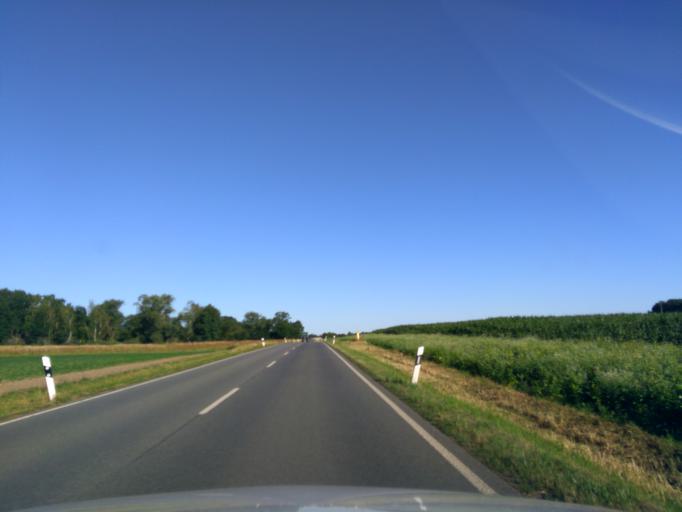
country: DE
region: Brandenburg
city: Fehrbellin
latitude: 52.7635
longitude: 12.8618
